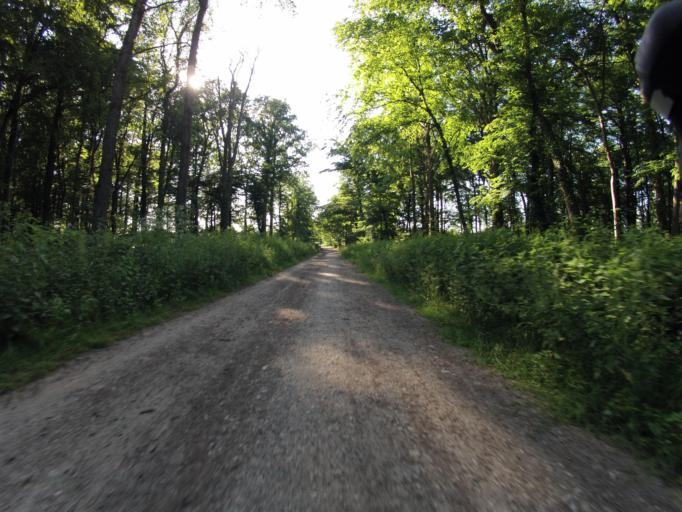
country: DE
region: Lower Saxony
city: Suddendorf
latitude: 52.3102
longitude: 7.2657
